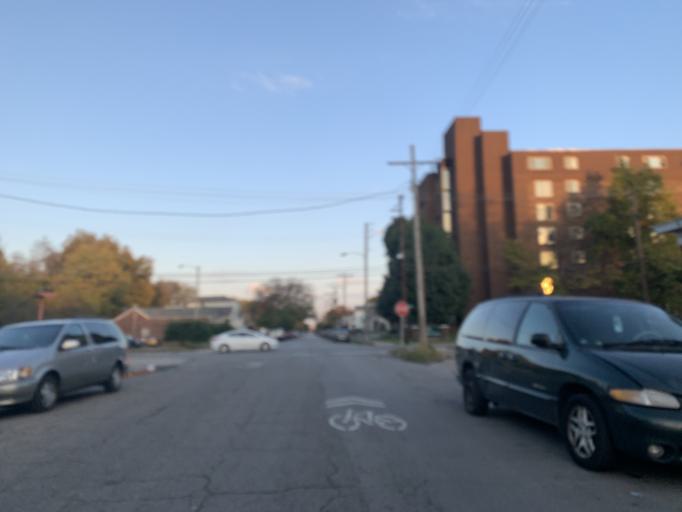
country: US
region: Kentucky
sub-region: Jefferson County
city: Louisville
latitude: 38.2542
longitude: -85.7949
